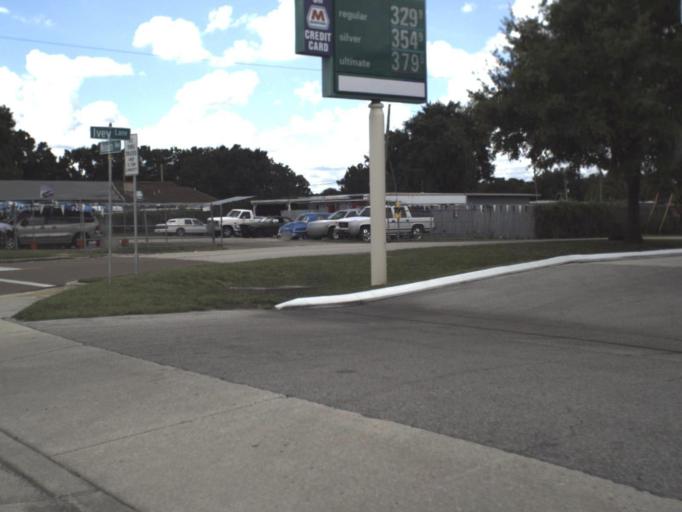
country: US
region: Florida
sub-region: Polk County
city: Winston
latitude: 28.0493
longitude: -81.9902
